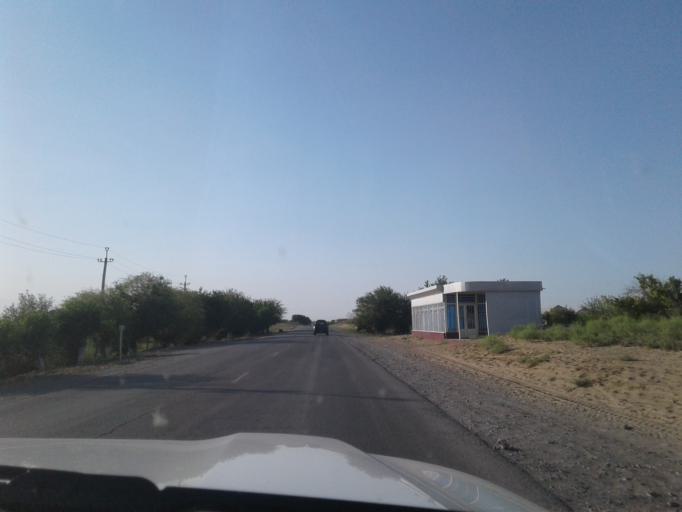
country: TM
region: Mary
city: Yoloeten
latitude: 37.2664
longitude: 62.3616
